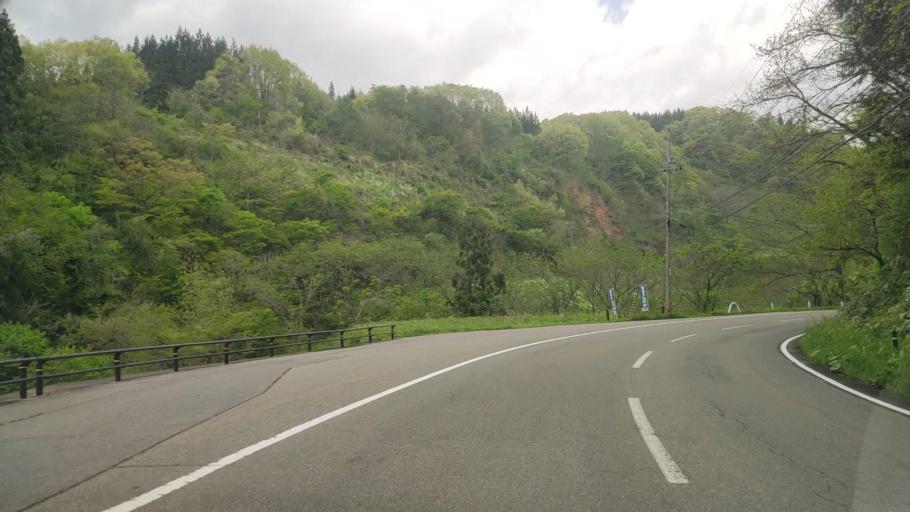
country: JP
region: Fukushima
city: Kitakata
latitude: 37.6601
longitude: 139.5880
